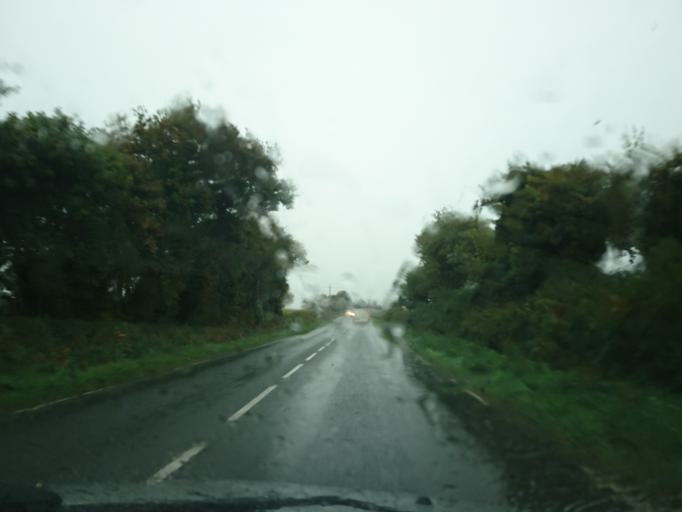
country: FR
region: Brittany
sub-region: Departement du Finistere
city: Gouesnou
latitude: 48.4720
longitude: -4.4420
